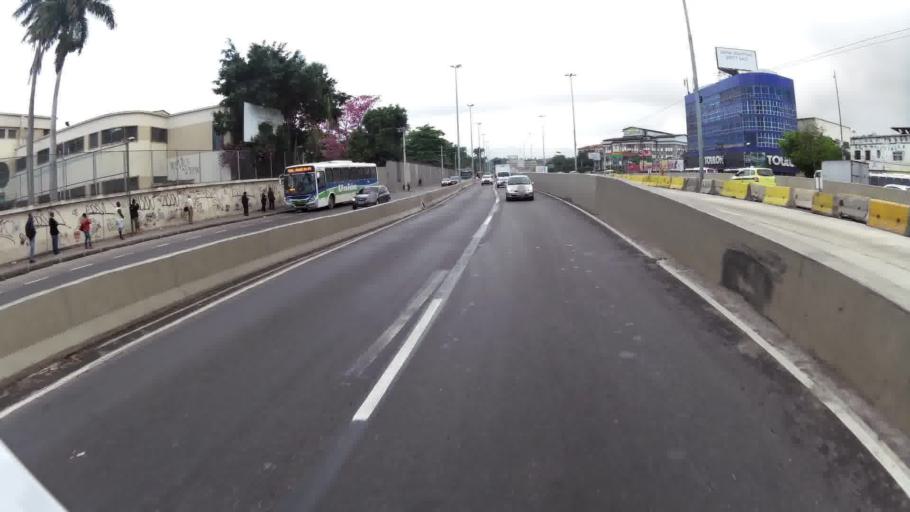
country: BR
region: Rio de Janeiro
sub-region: Rio De Janeiro
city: Rio de Janeiro
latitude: -22.8644
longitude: -43.2478
